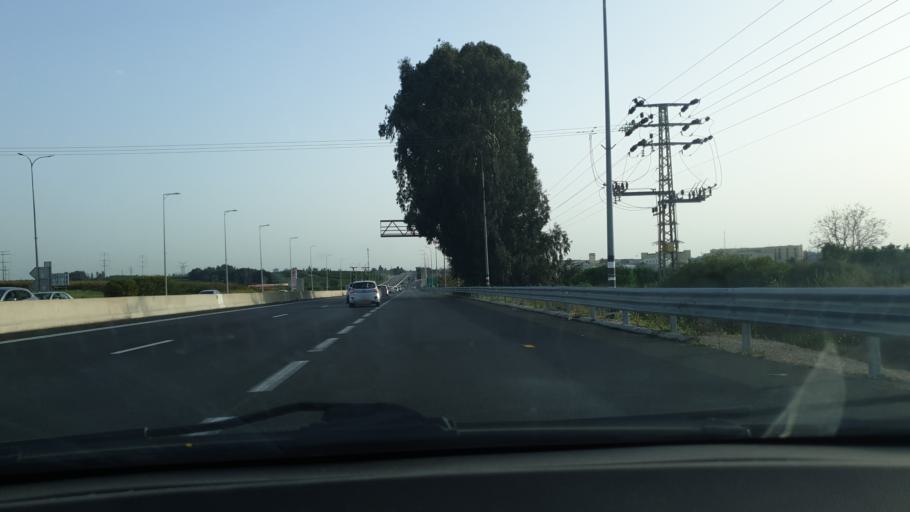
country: IL
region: Central District
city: Even Yehuda
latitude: 32.2469
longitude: 34.8886
